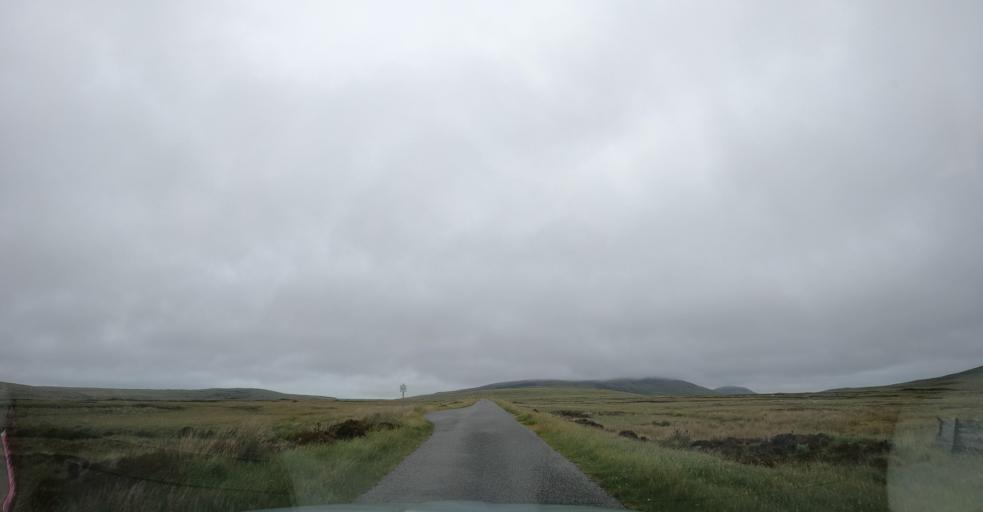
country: GB
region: Scotland
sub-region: Eilean Siar
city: Isle of North Uist
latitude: 57.5878
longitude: -7.3943
